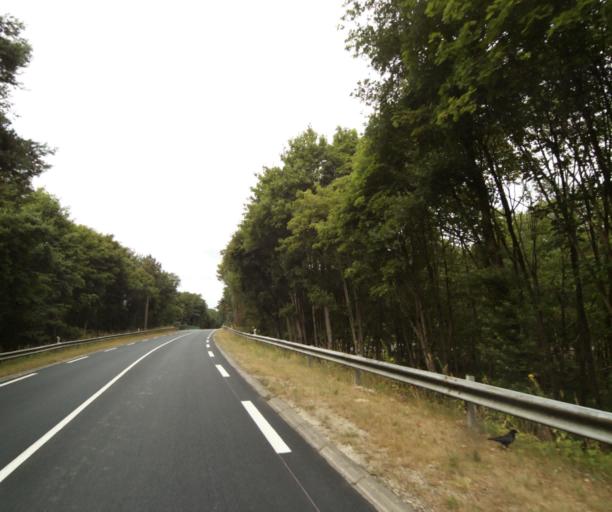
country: FR
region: Ile-de-France
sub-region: Departement de Seine-et-Marne
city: Arbonne-la-Foret
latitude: 48.4031
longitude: 2.5564
